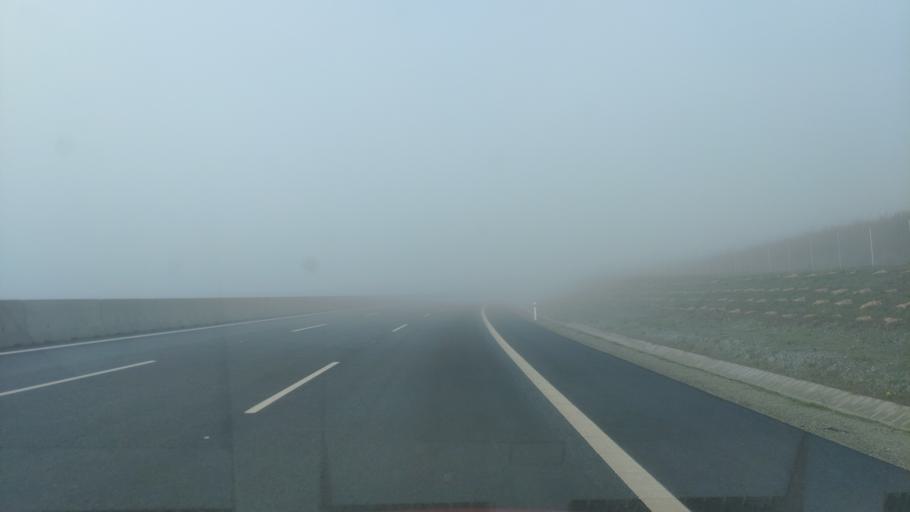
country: SK
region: Kosicky
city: Kosice
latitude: 48.7282
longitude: 21.4146
